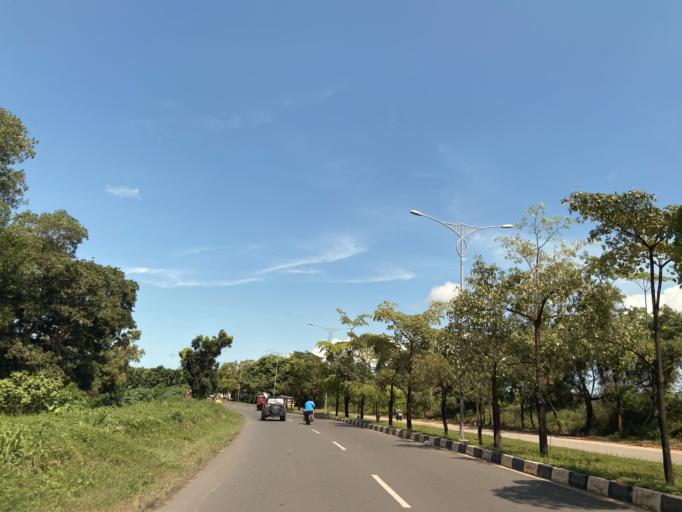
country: SG
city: Singapore
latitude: 1.1115
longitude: 104.0583
